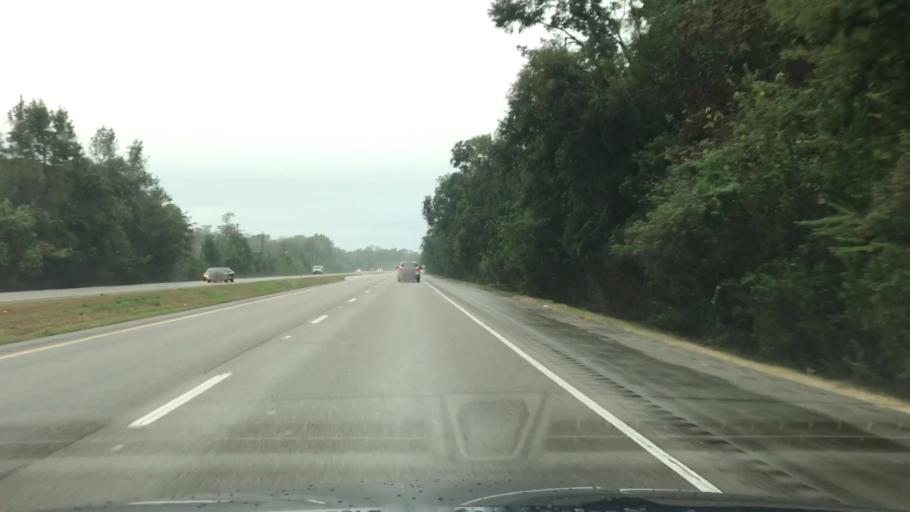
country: US
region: Louisiana
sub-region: Saint Charles Parish
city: Paradis
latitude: 29.8494
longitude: -90.4479
